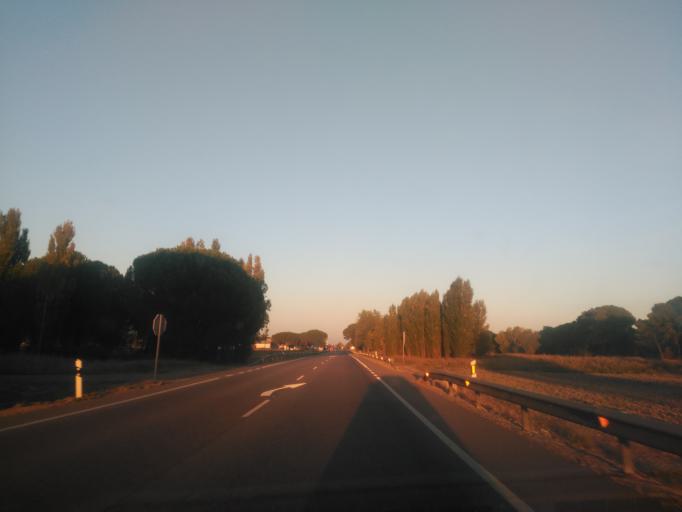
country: ES
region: Castille and Leon
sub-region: Provincia de Valladolid
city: Sardon de Duero
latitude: 41.6057
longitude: -4.4477
